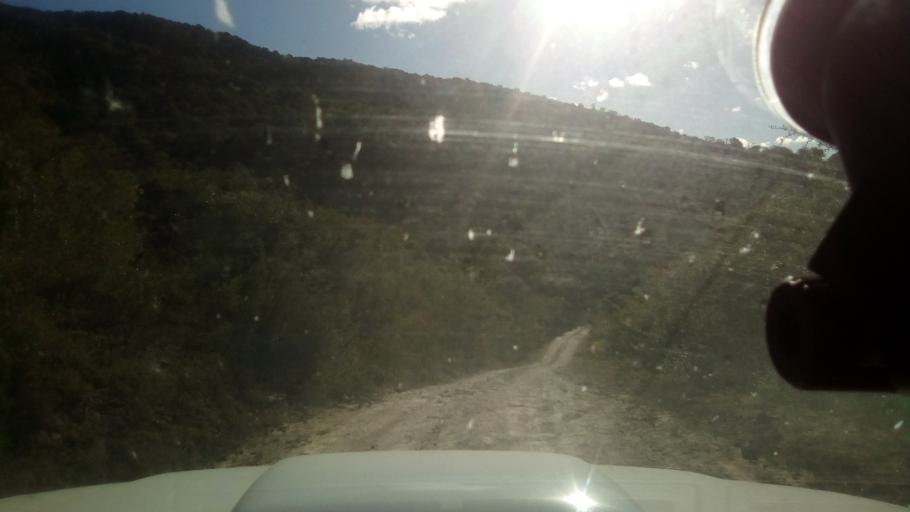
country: ZA
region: Eastern Cape
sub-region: Buffalo City Metropolitan Municipality
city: Bhisho
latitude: -32.7359
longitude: 27.3466
